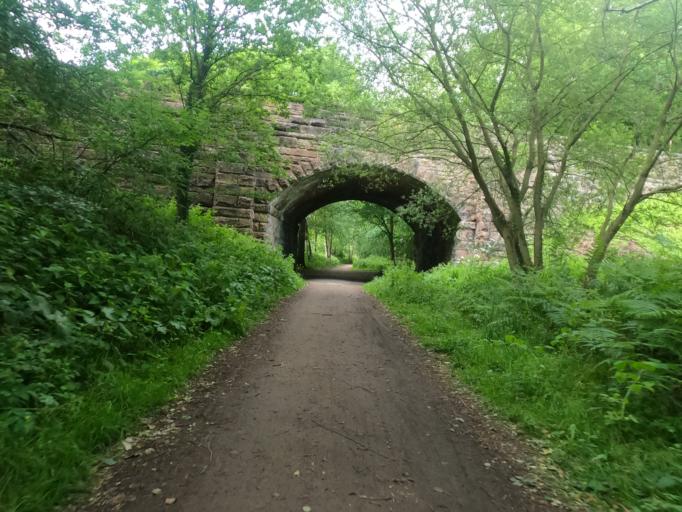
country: GB
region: England
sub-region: Cheshire West and Chester
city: Cuddington
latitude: 53.2266
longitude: -2.6197
